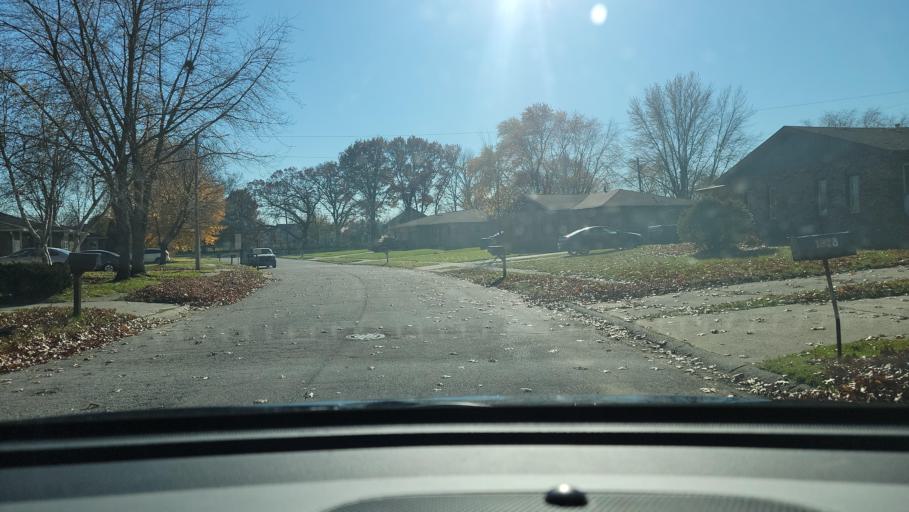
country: US
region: Indiana
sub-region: Porter County
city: Portage
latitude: 41.5962
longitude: -87.1507
